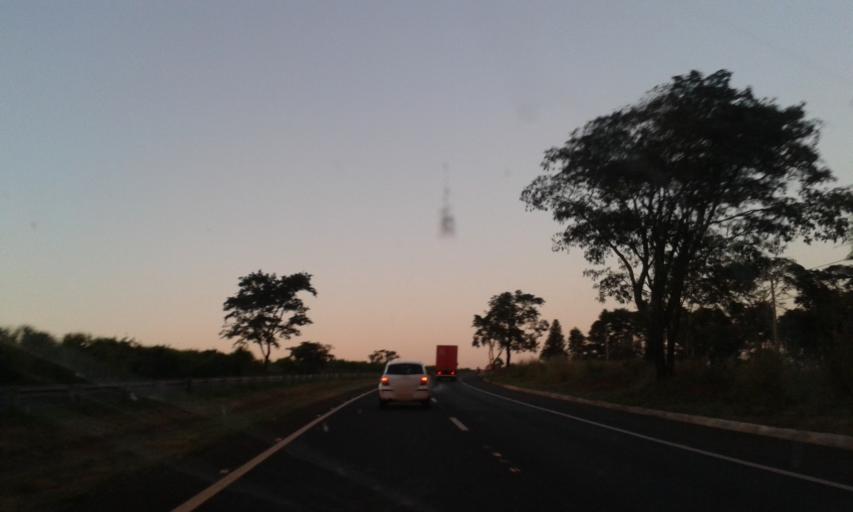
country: BR
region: Minas Gerais
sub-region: Monte Alegre De Minas
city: Monte Alegre de Minas
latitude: -18.8674
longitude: -48.5945
